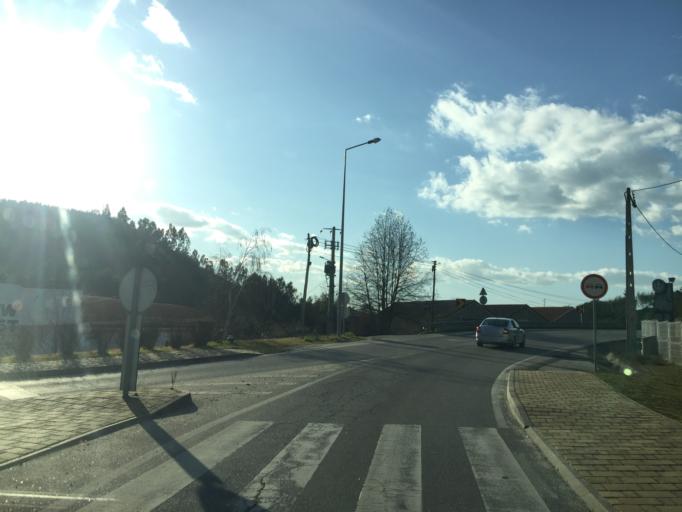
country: PT
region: Guarda
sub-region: Seia
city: Seia
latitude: 40.4325
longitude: -7.7189
